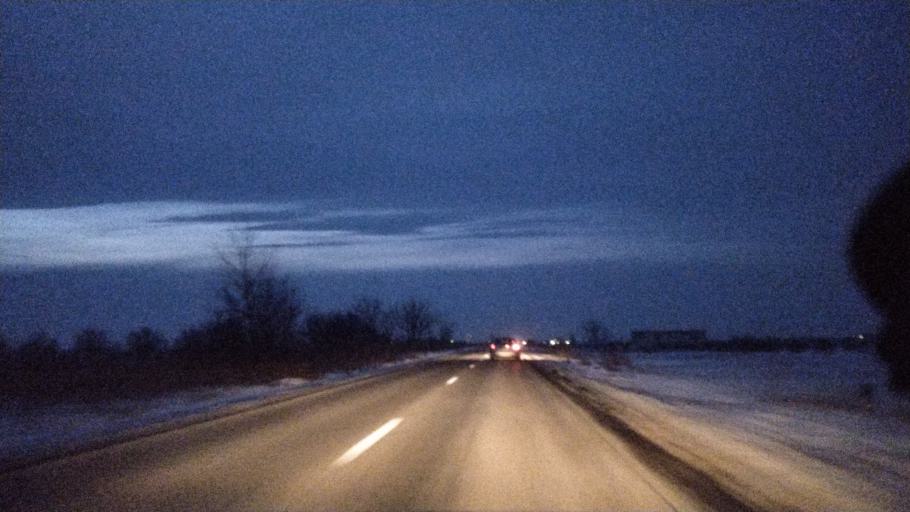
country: RO
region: Vrancea
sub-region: Comuna Milcovul
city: Milcovul
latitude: 45.6689
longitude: 27.2632
